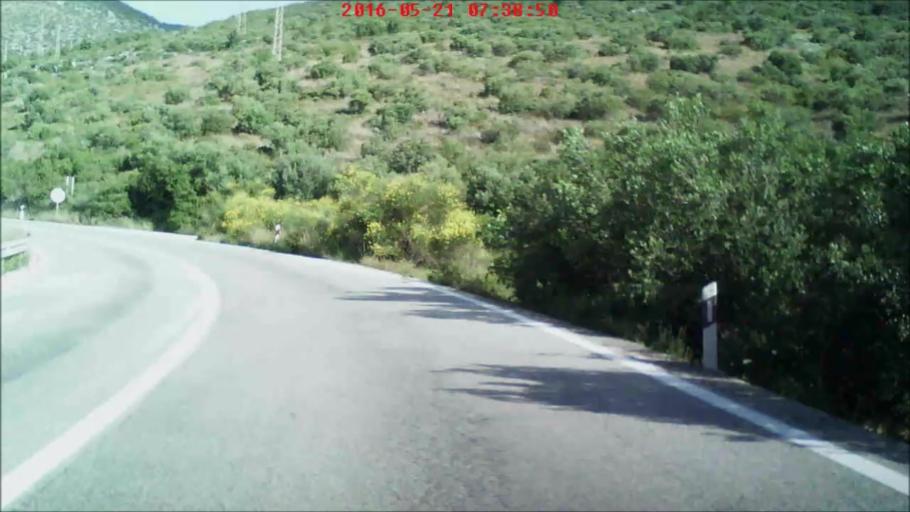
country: HR
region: Dubrovacko-Neretvanska
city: Podgora
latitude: 42.8030
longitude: 17.8471
